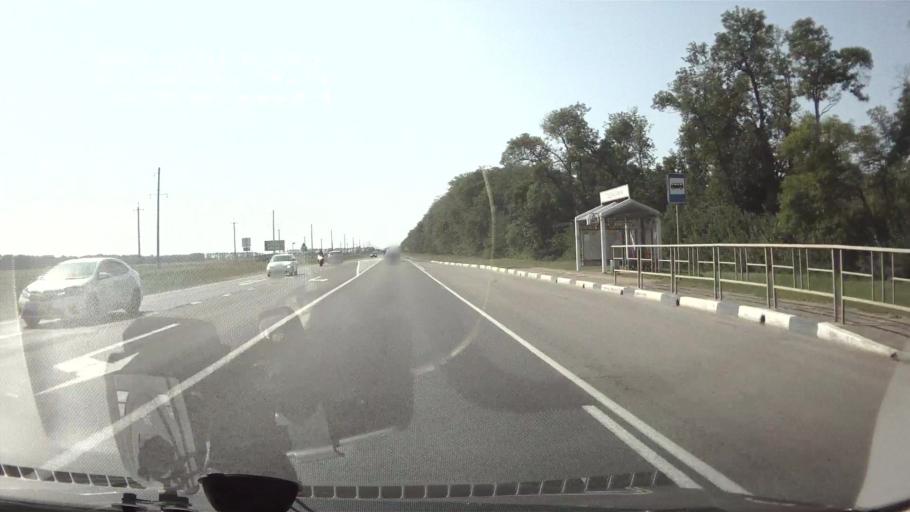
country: RU
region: Krasnodarskiy
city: Starokorsunskaya
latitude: 45.0485
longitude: 39.2816
